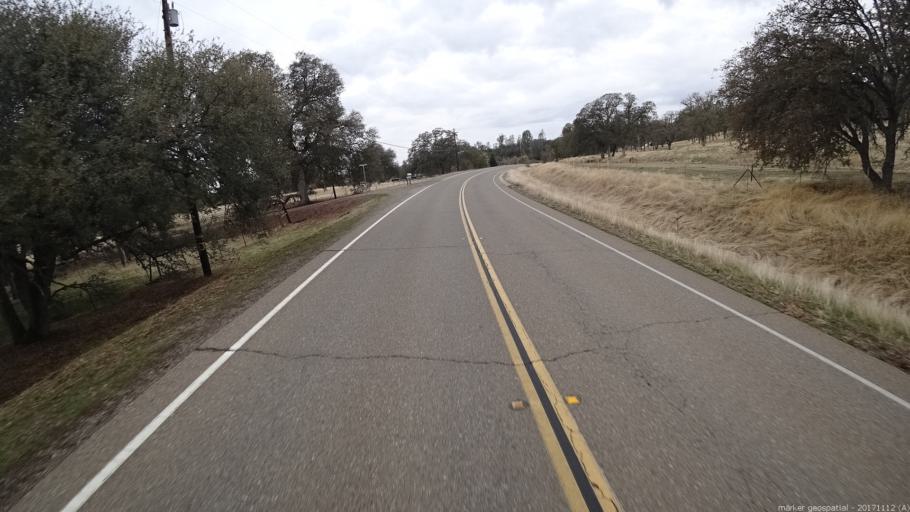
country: US
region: California
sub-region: Shasta County
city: Palo Cedro
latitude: 40.4856
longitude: -122.1478
